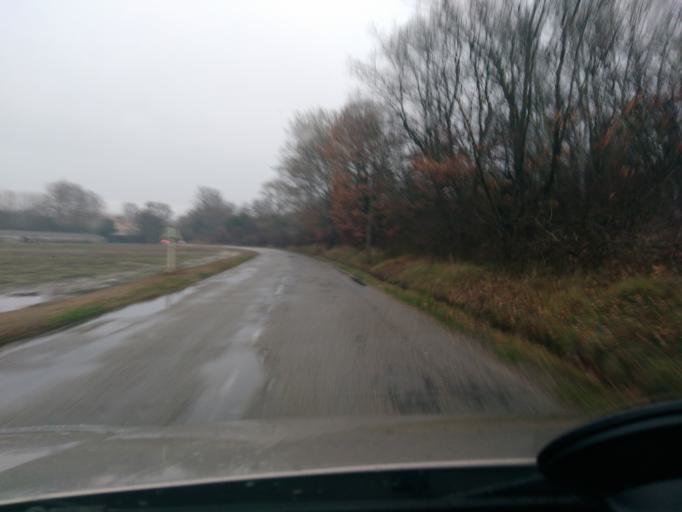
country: FR
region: Rhone-Alpes
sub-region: Departement de l'Ardeche
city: Le Teil
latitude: 44.5505
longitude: 4.7134
